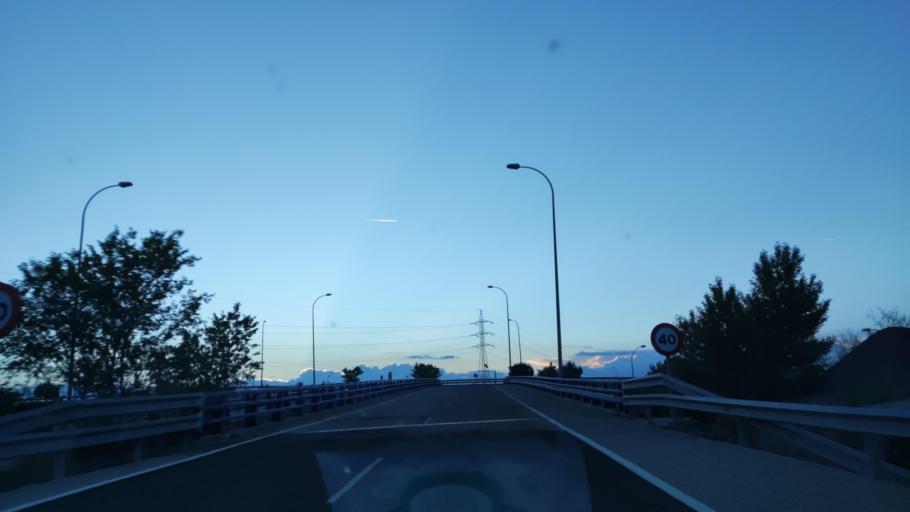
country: ES
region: Madrid
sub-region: Provincia de Madrid
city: San Sebastian de los Reyes
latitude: 40.5238
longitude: -3.5973
